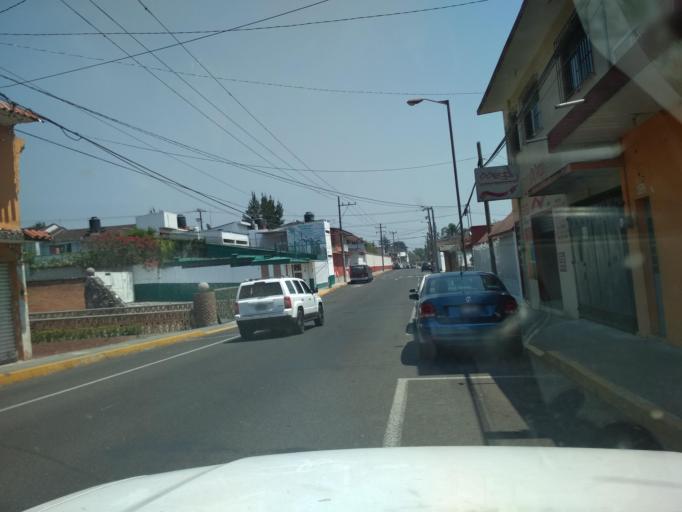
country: MX
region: Veracruz
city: Orizaba
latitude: 18.8520
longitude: -97.0884
